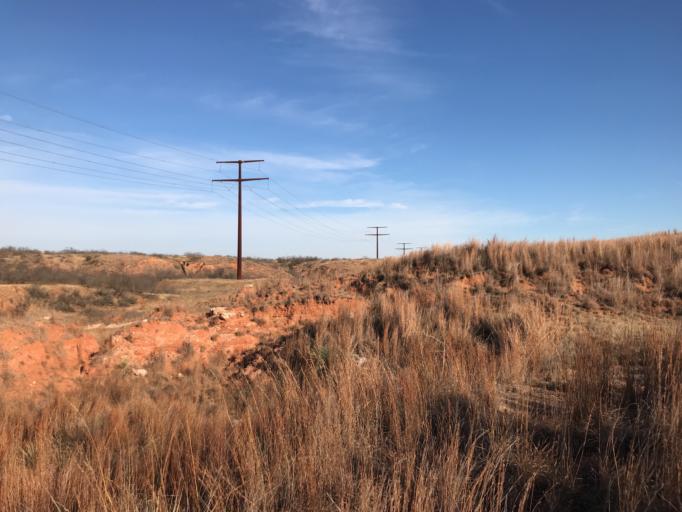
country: US
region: Texas
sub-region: Childress County
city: Childress
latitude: 34.3341
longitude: -100.4806
